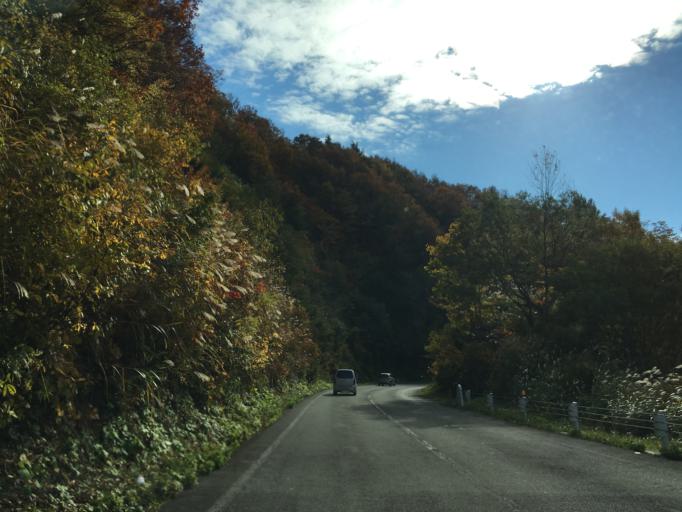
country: JP
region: Fukushima
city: Inawashiro
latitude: 37.6742
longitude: 140.1162
